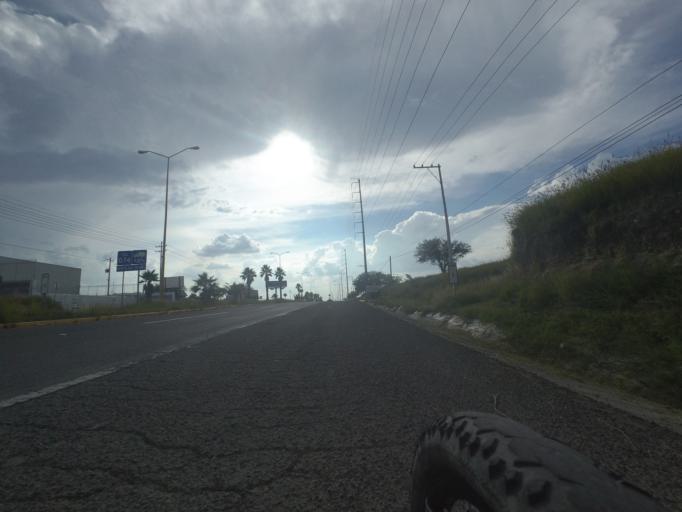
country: MX
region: Aguascalientes
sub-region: Aguascalientes
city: Penuelas (El Cienegal)
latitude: 21.7246
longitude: -102.2861
